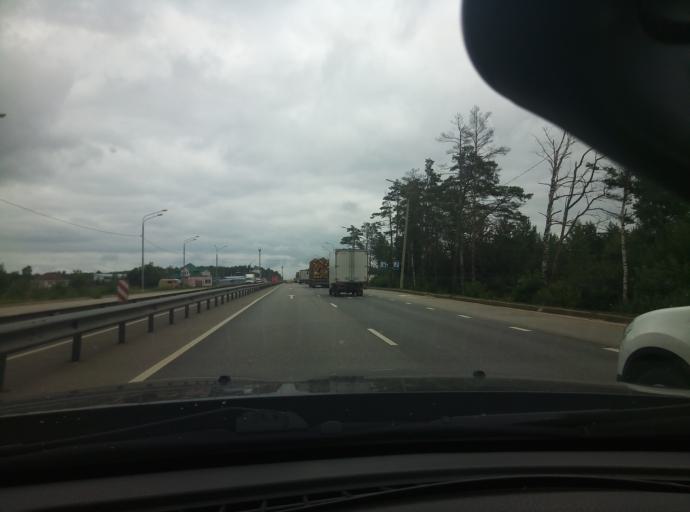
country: RU
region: Kaluga
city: Obninsk
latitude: 55.0729
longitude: 36.6265
